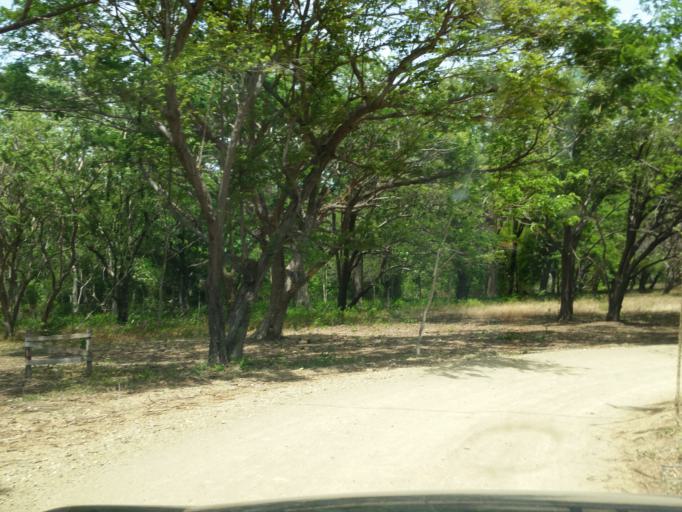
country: NI
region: Rivas
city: Tola
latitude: 11.4139
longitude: -86.0453
